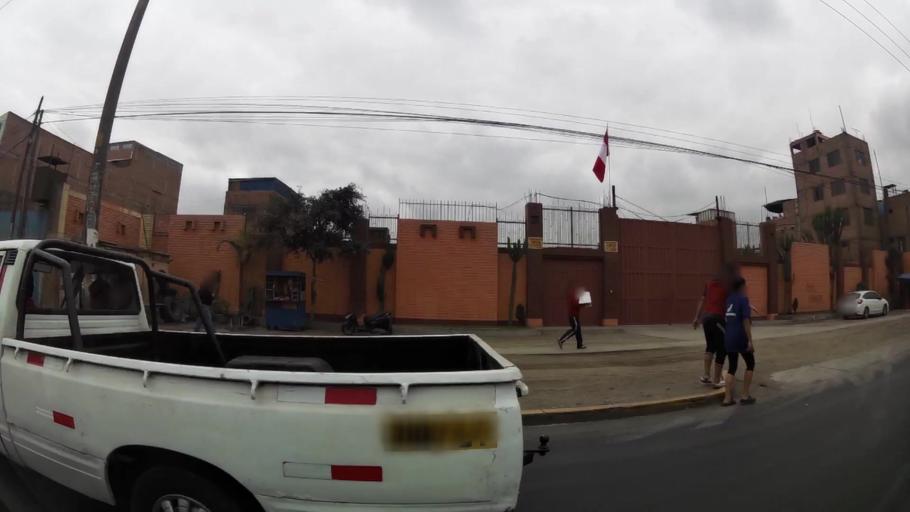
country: PE
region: Lima
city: Lima
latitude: -12.0456
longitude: -77.0671
